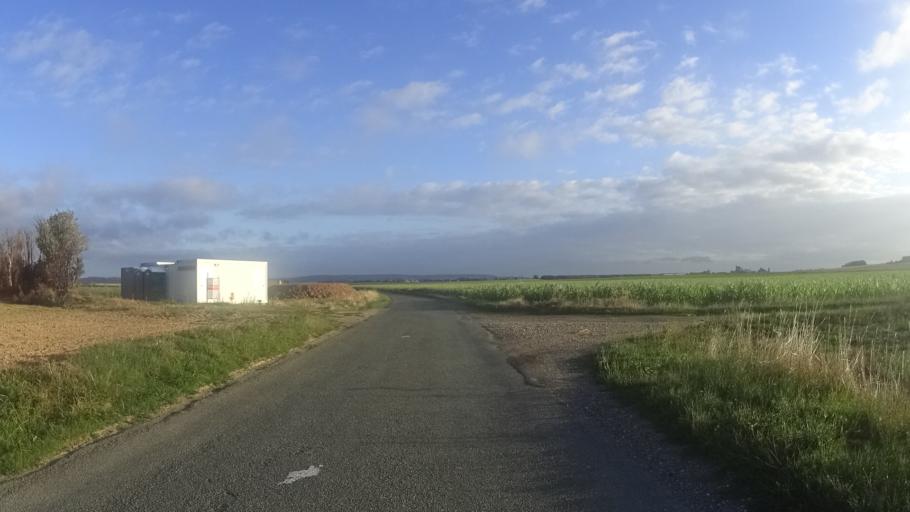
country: FR
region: Picardie
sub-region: Departement de l'Oise
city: Chamant
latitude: 49.1983
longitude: 2.6687
